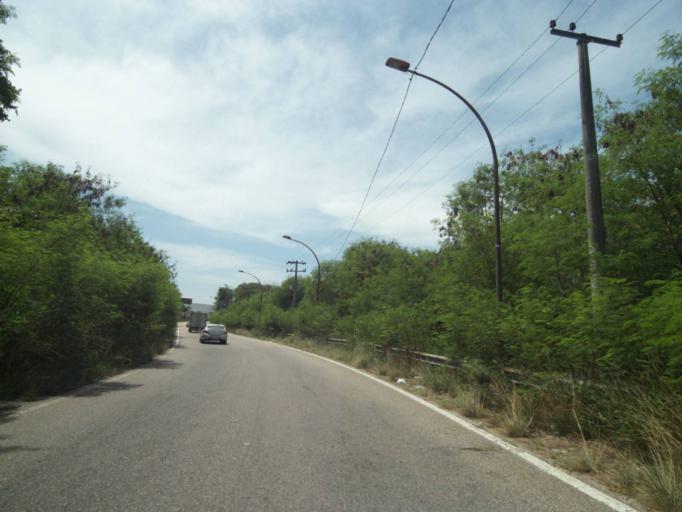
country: BR
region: Rio de Janeiro
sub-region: Duque De Caxias
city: Duque de Caxias
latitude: -22.8096
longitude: -43.2903
